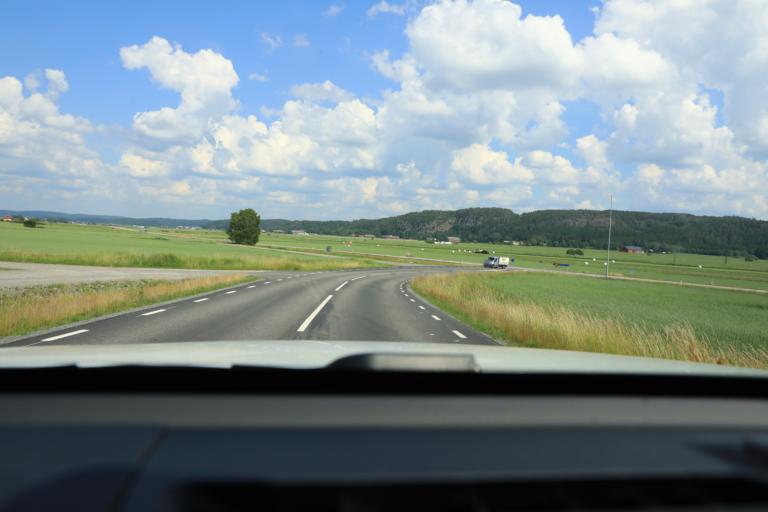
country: SE
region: Halland
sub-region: Varbergs Kommun
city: Veddige
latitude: 57.2100
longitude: 12.3072
